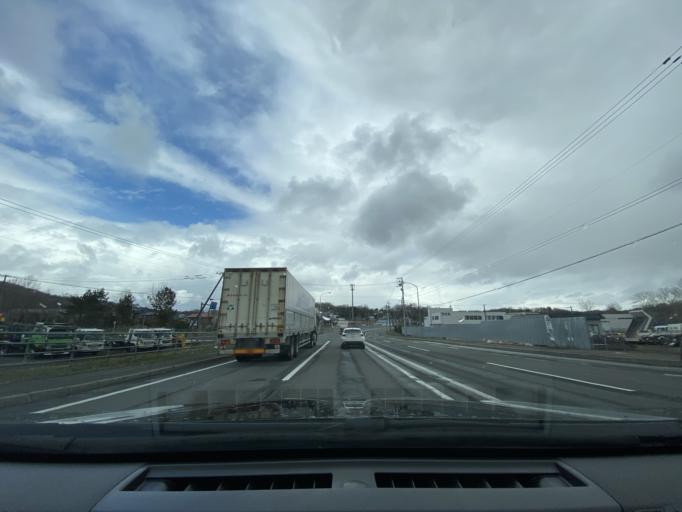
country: JP
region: Hokkaido
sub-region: Asahikawa-shi
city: Asahikawa
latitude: 43.7657
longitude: 142.2813
